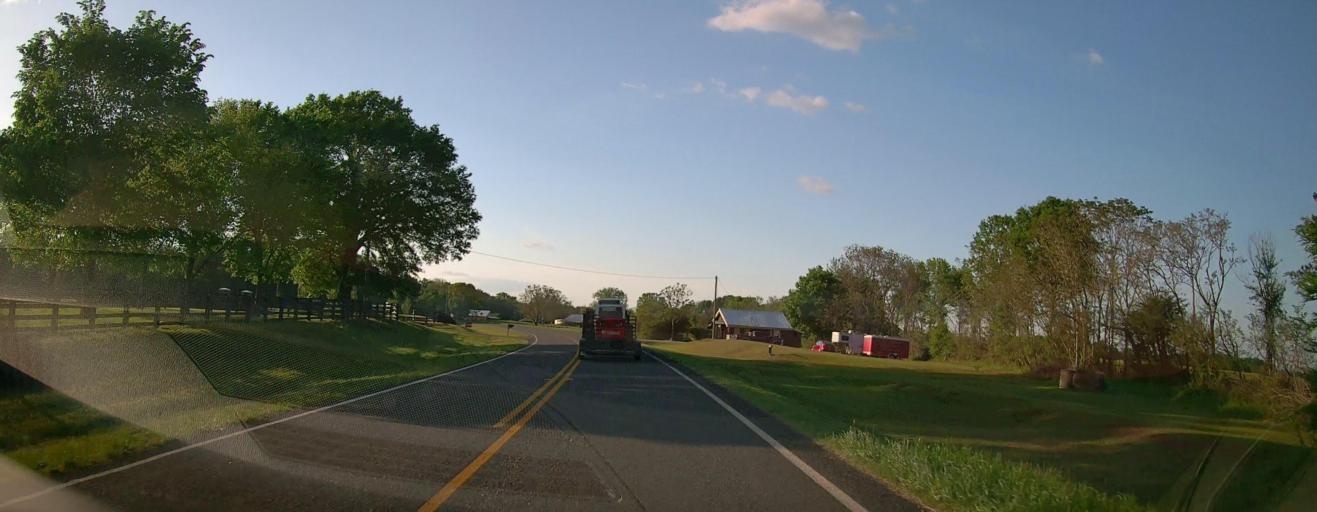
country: US
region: Georgia
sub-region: Walton County
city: Social Circle
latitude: 33.5010
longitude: -83.6518
